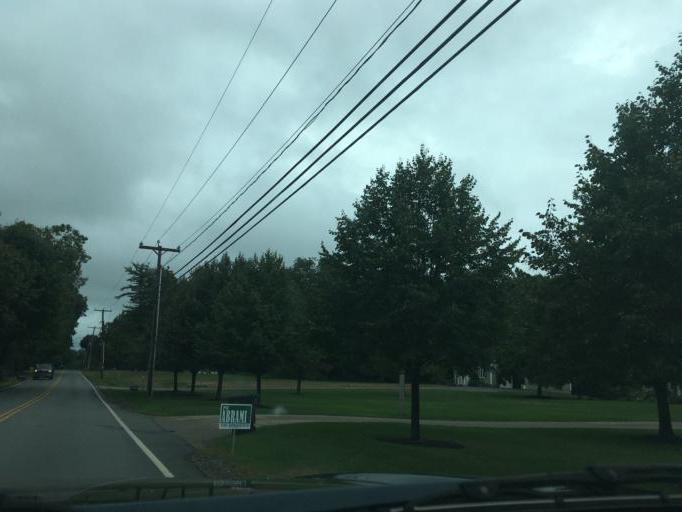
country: US
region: New Hampshire
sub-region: Rockingham County
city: Stratham Station
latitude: 43.0154
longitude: -70.8857
